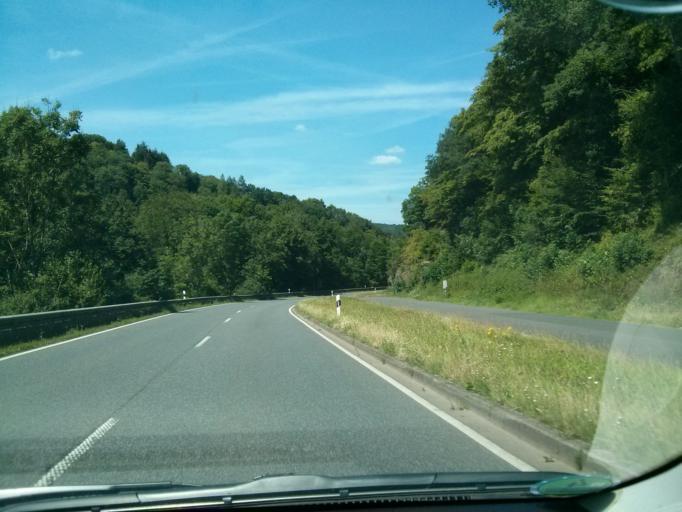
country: DE
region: Rheinland-Pfalz
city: Honningen
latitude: 50.4589
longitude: 6.9490
